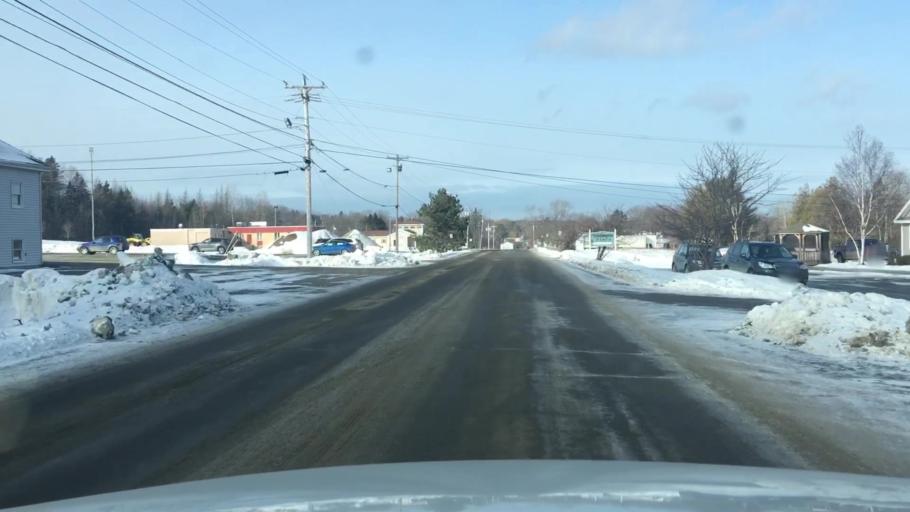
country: US
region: Maine
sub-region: Washington County
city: Calais
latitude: 45.1793
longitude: -67.2663
